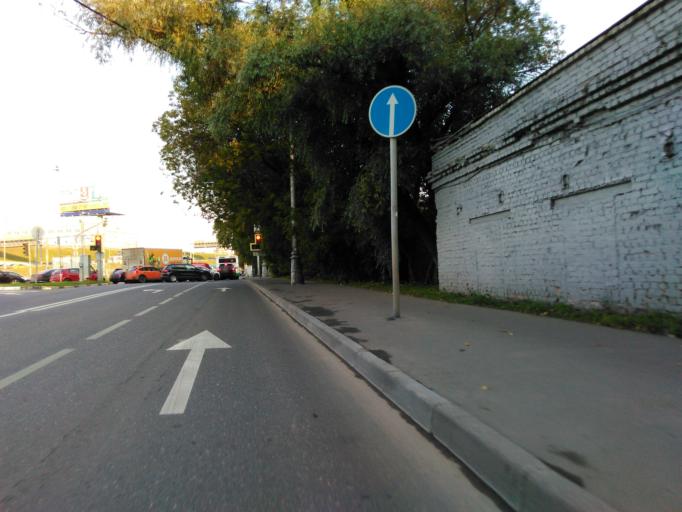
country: RU
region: Moscow
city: Vorob'yovo
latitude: 55.7315
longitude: 37.5414
